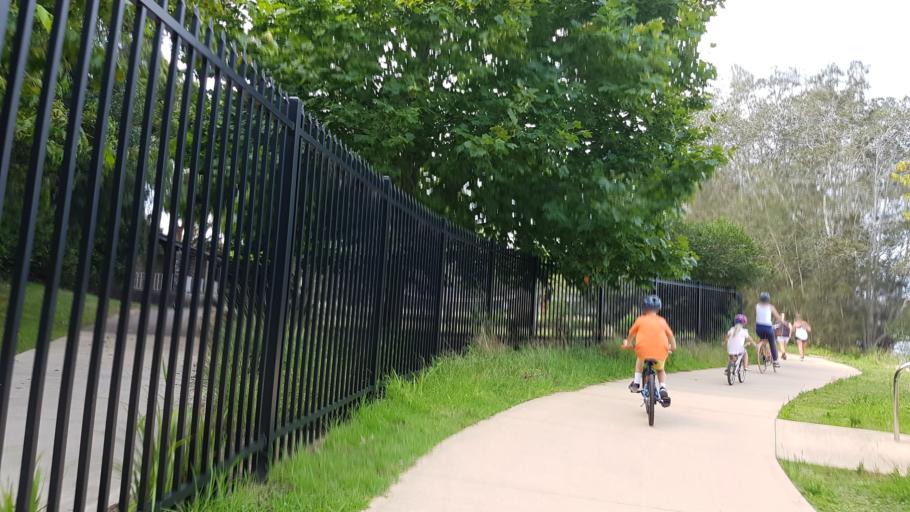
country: AU
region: New South Wales
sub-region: Pittwater
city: North Narrabeen
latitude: -33.7200
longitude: 151.2712
